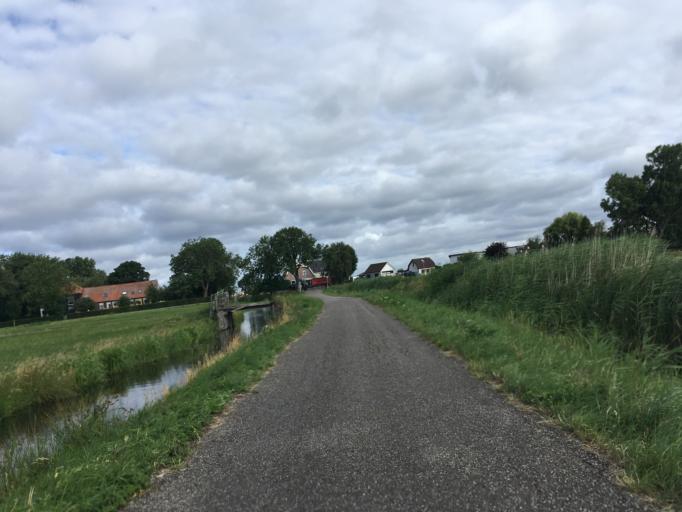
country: NL
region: North Holland
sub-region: Gemeente Haarlem
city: Haarlem
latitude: 52.3949
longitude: 4.6923
